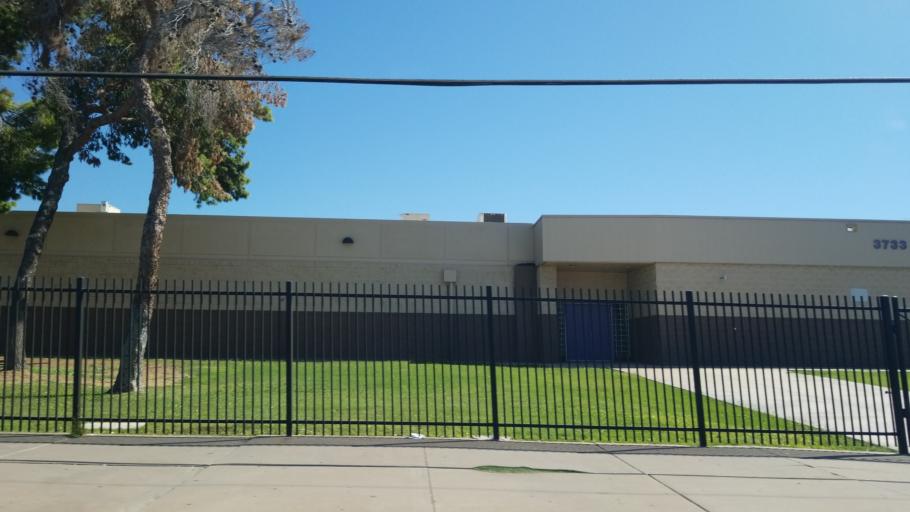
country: US
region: Arizona
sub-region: Maricopa County
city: Tolleson
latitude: 33.4908
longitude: -112.2205
